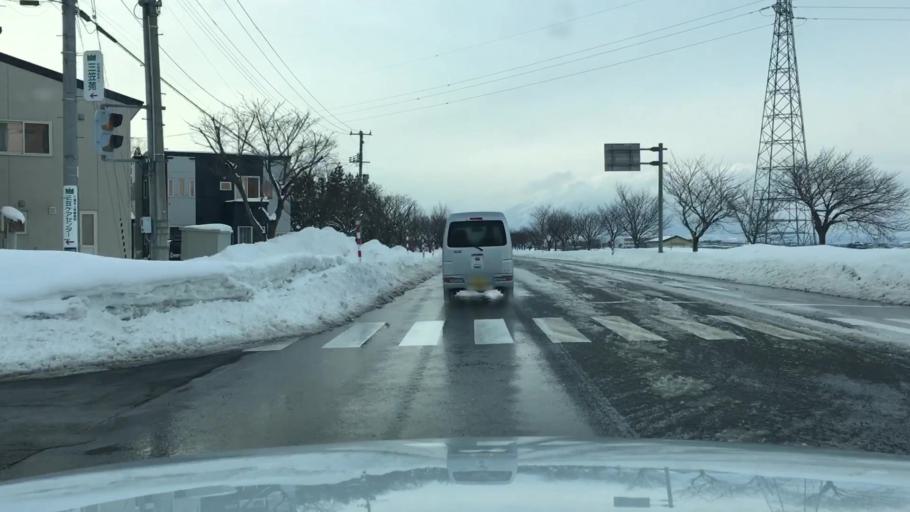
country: JP
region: Aomori
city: Kuroishi
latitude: 40.5927
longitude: 140.5493
